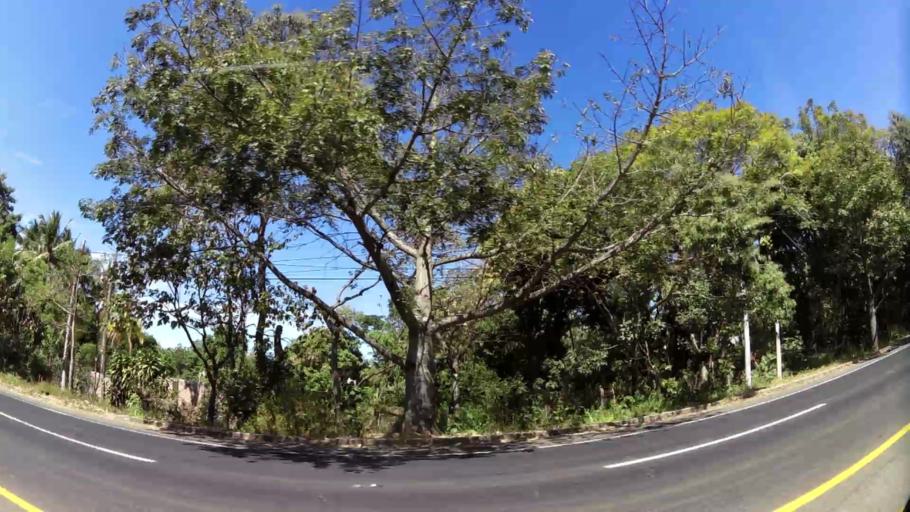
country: SV
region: Santa Ana
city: Chalchuapa
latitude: 13.9728
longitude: -89.7103
